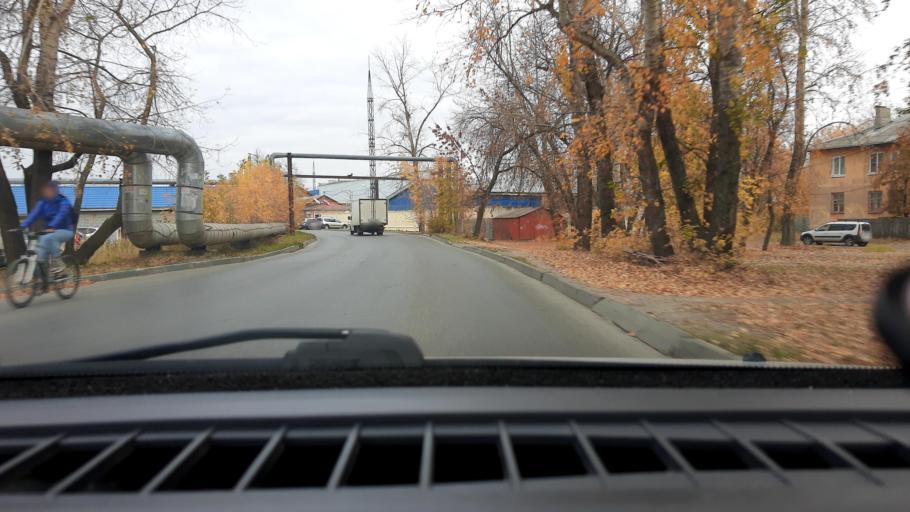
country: RU
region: Nizjnij Novgorod
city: Gorbatovka
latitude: 56.3423
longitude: 43.8240
